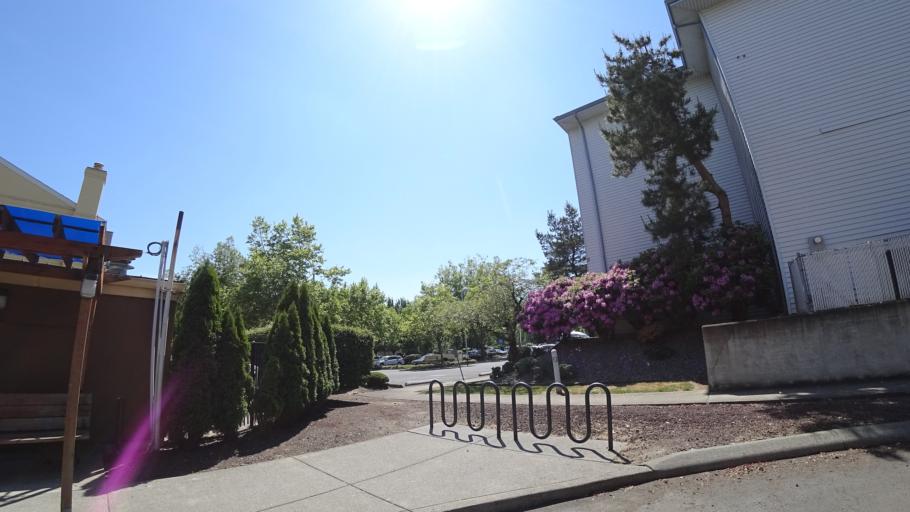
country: US
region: Washington
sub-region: Clark County
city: Mill Plain
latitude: 45.5678
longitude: -122.5406
